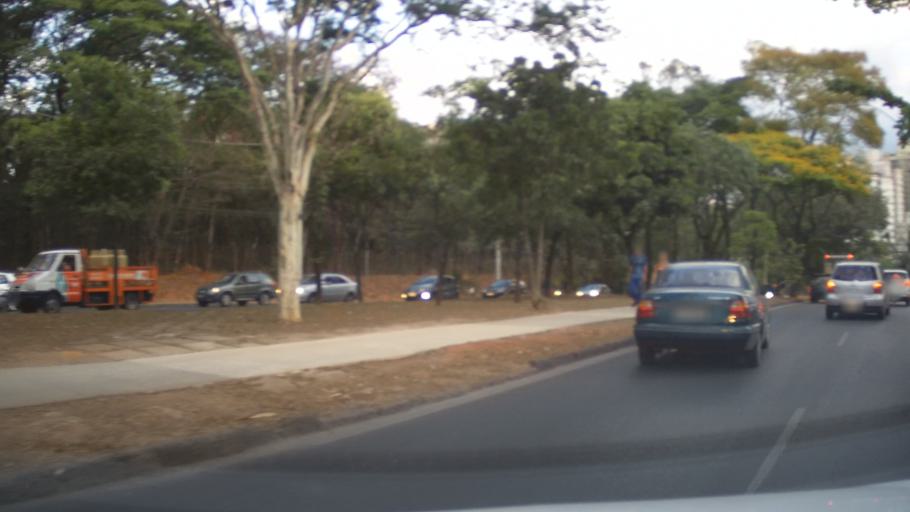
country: BR
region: Minas Gerais
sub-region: Belo Horizonte
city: Belo Horizonte
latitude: -19.8909
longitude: -43.9203
